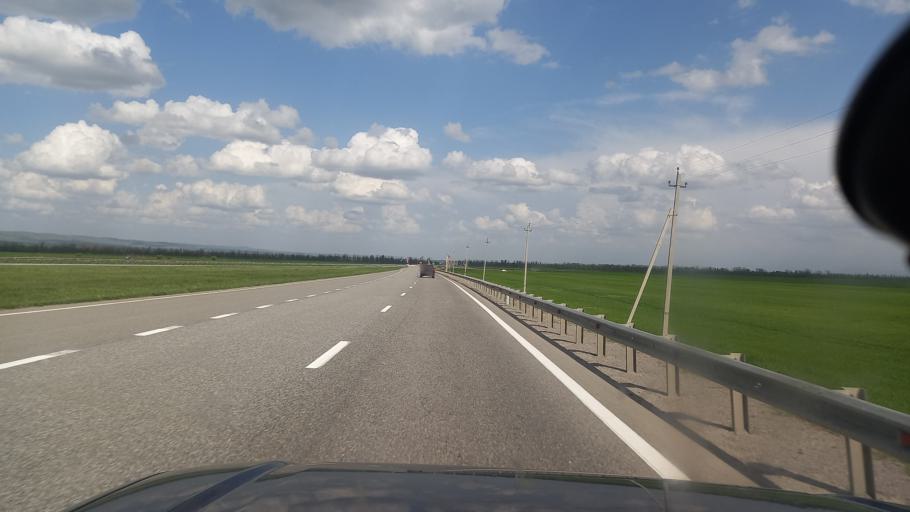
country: RU
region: Ingushetiya
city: Sernovodsk
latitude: 43.2755
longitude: 45.1364
